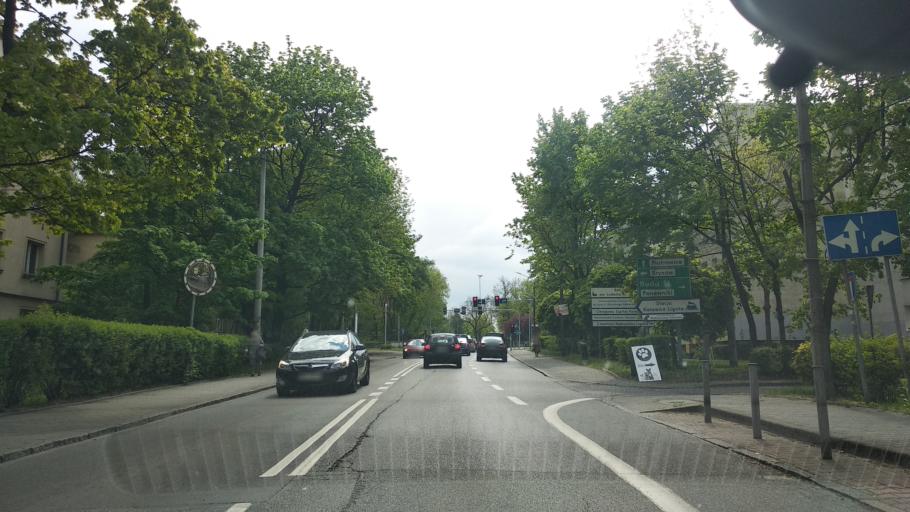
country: PL
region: Silesian Voivodeship
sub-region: Katowice
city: Katowice
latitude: 50.2270
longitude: 18.9700
